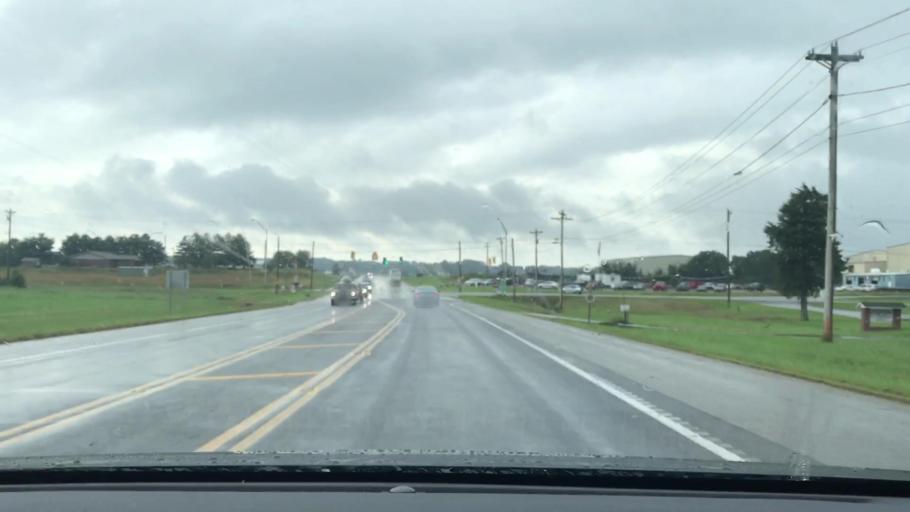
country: US
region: Tennessee
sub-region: Macon County
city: Lafayette
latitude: 36.5290
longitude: -86.0631
